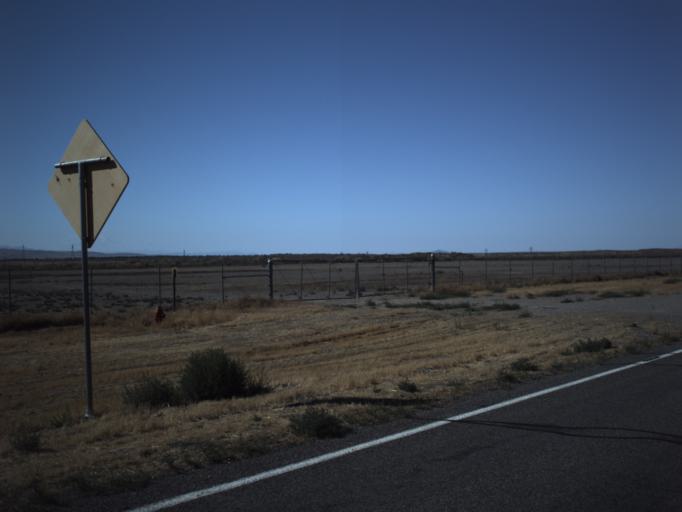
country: US
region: Utah
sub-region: Millard County
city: Delta
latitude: 39.5110
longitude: -112.3785
